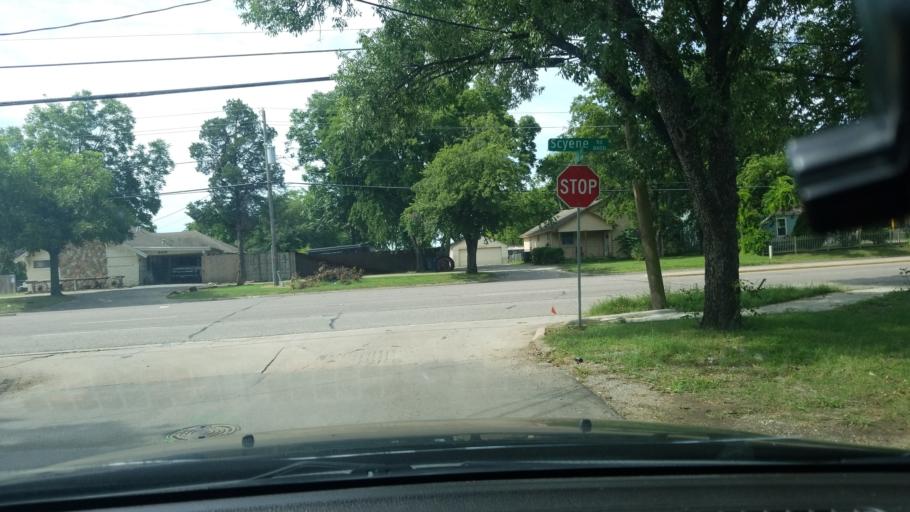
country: US
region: Texas
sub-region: Dallas County
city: Balch Springs
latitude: 32.7638
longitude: -96.6750
